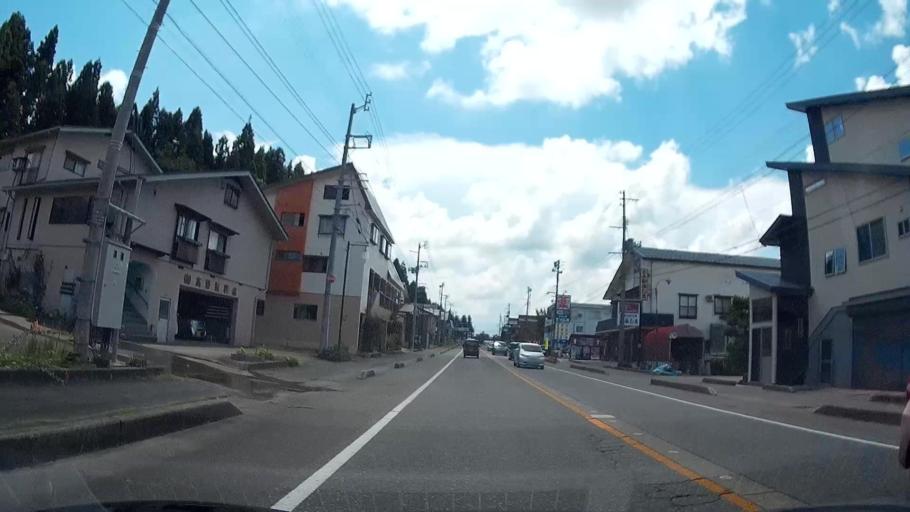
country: JP
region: Niigata
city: Tokamachi
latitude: 37.0939
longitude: 138.7287
